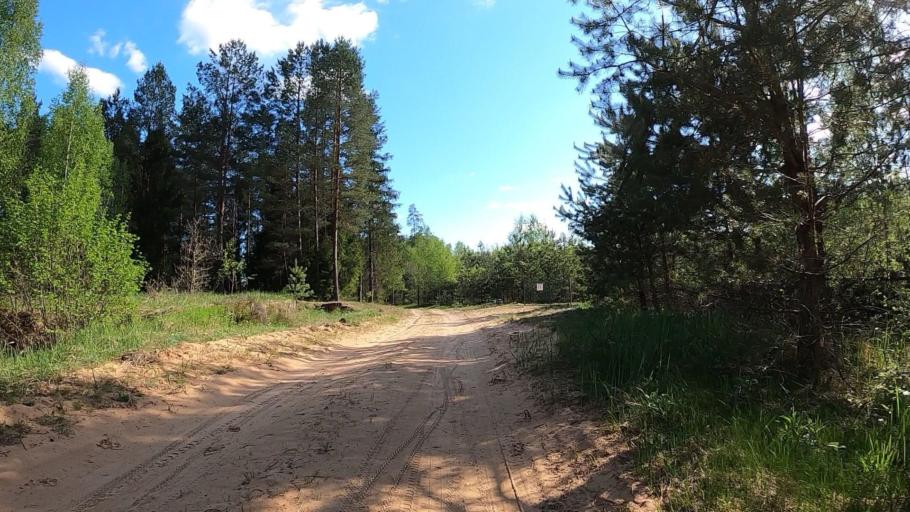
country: LV
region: Baldone
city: Baldone
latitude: 56.7729
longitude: 24.4289
